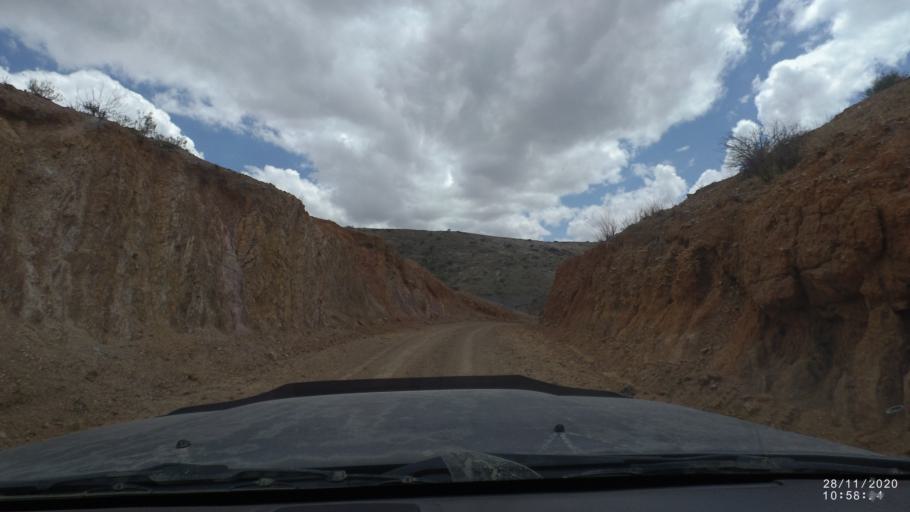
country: BO
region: Cochabamba
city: Capinota
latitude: -17.7750
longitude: -66.1124
